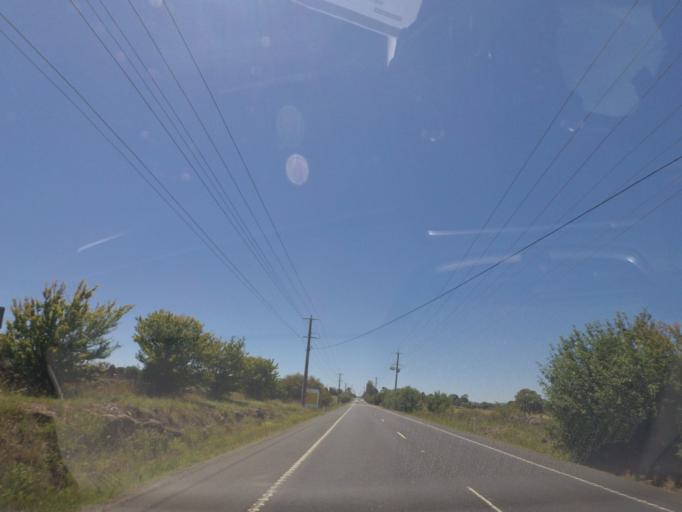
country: AU
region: Victoria
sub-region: Whittlesea
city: Mernda
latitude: -37.5805
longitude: 145.0330
